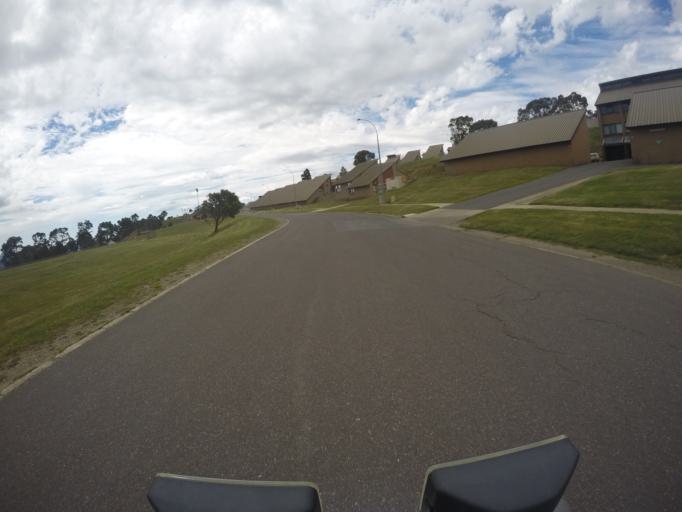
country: AU
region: New South Wales
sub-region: Snowy River
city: Jindabyne
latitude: -35.9357
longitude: 148.3805
